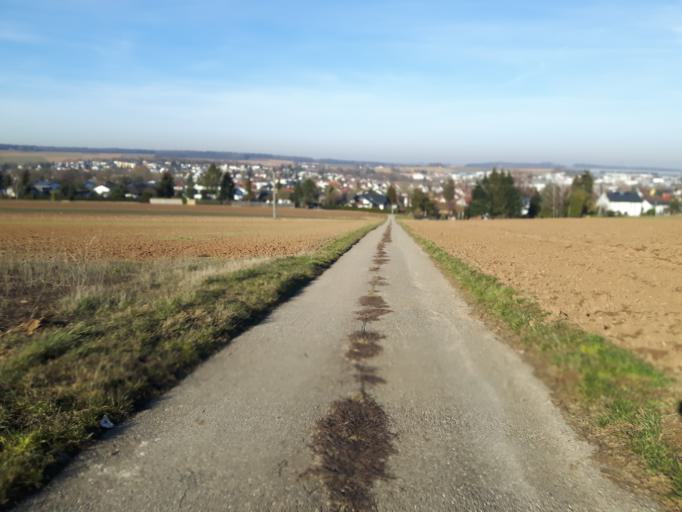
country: DE
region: Baden-Wuerttemberg
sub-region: Regierungsbezirk Stuttgart
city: Leingarten
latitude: 49.1376
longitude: 9.1139
